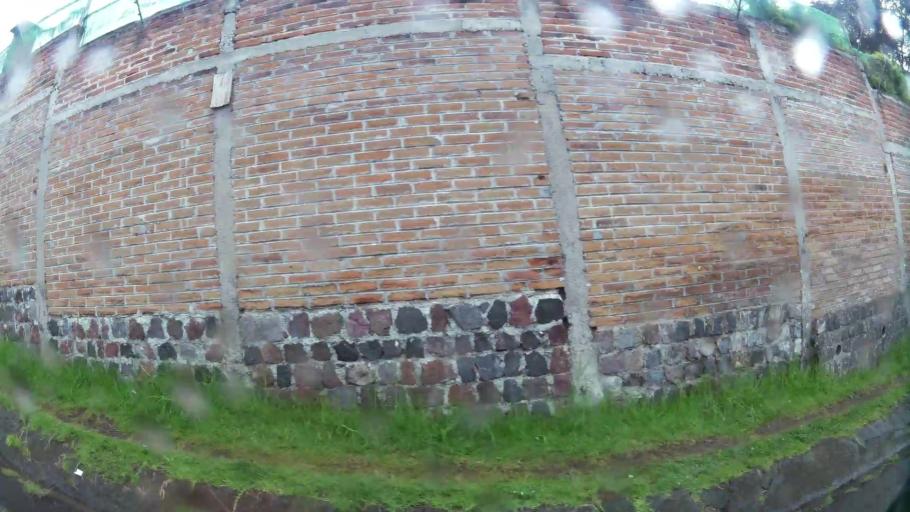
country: EC
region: Pichincha
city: Sangolqui
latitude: -0.2823
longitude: -78.4671
